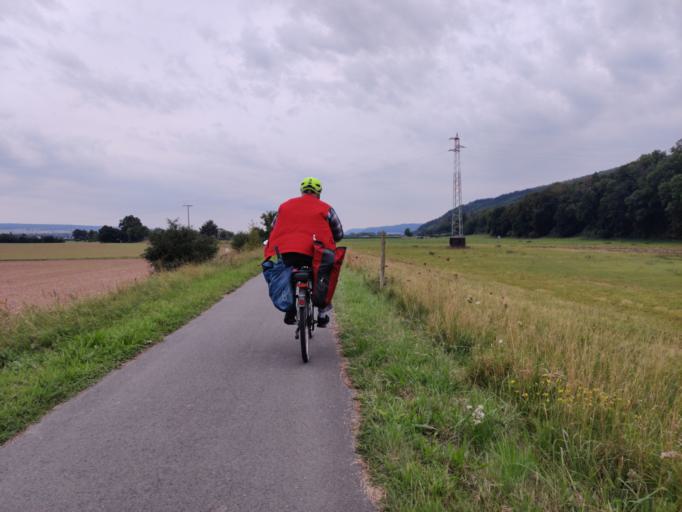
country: DE
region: Lower Saxony
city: Bevern
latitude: 51.8650
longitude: 9.4627
